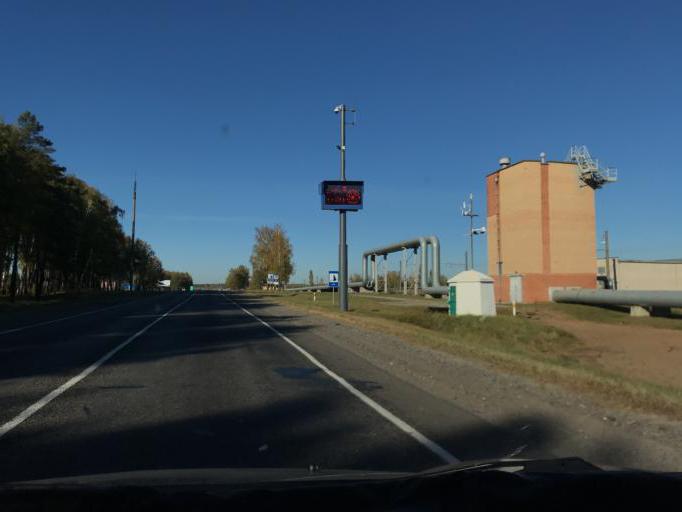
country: BY
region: Gomel
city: Mazyr
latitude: 51.9957
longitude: 29.2583
